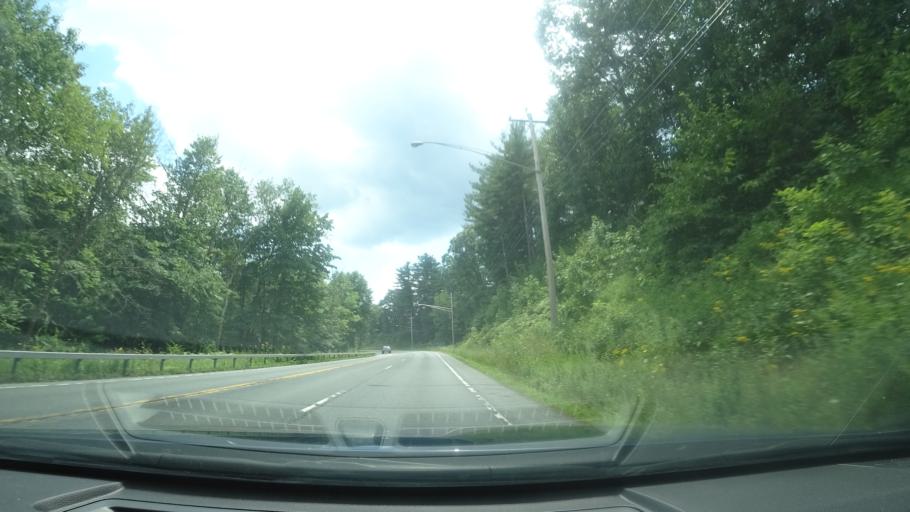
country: US
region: New York
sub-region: Warren County
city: Glens Falls North
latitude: 43.3993
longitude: -73.7050
